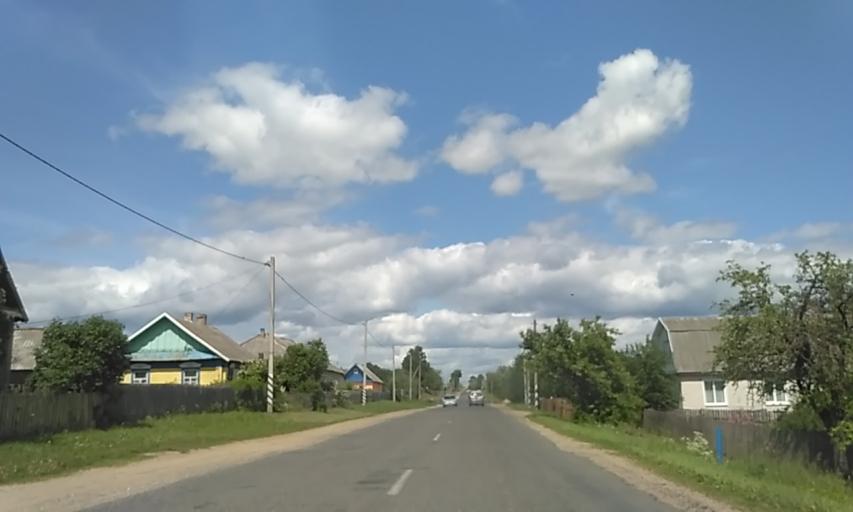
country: BY
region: Minsk
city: Krupki
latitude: 54.3435
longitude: 29.1489
